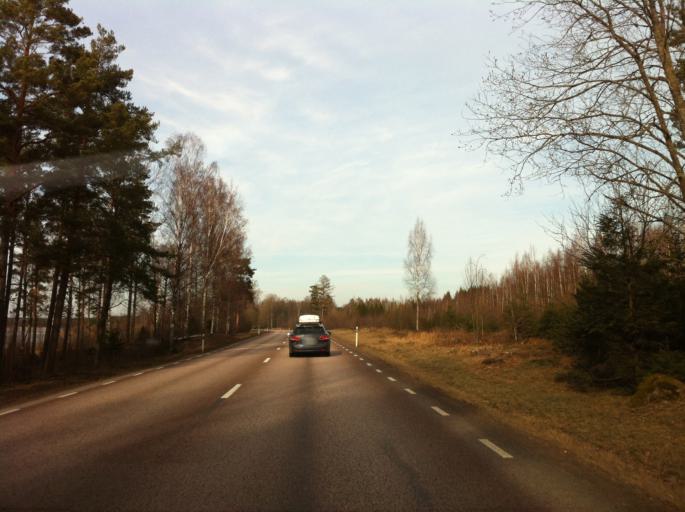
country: SE
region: Vaestra Goetaland
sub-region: Gullspangs Kommun
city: Gullspang
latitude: 59.0601
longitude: 14.1488
